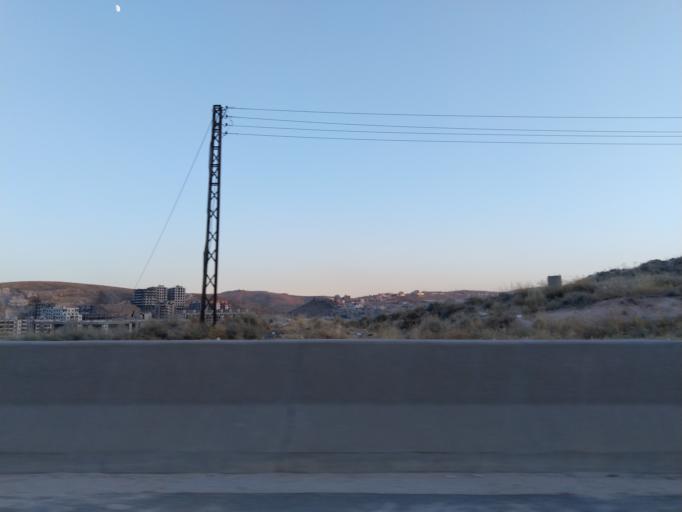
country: SY
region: Rif-dimashq
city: At Tall
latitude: 33.5856
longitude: 36.3023
